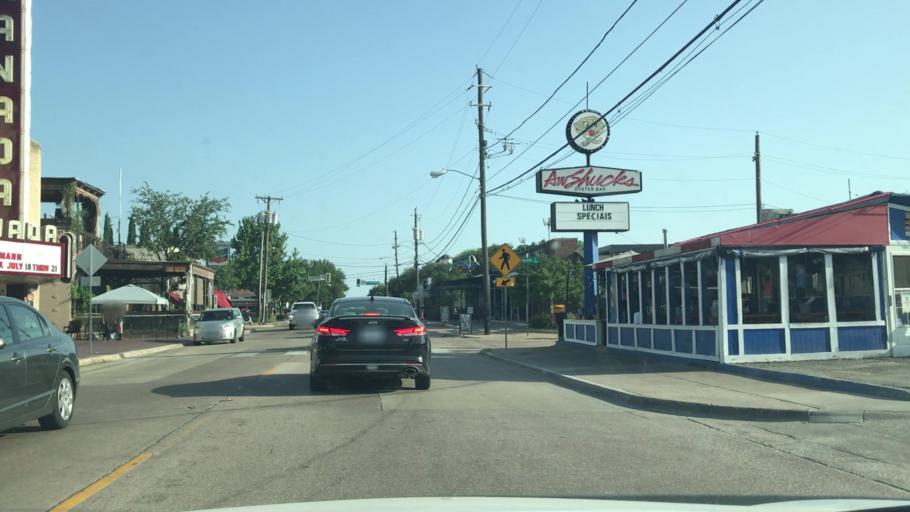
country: US
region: Texas
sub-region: Dallas County
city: Highland Park
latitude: 32.8312
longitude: -96.7702
